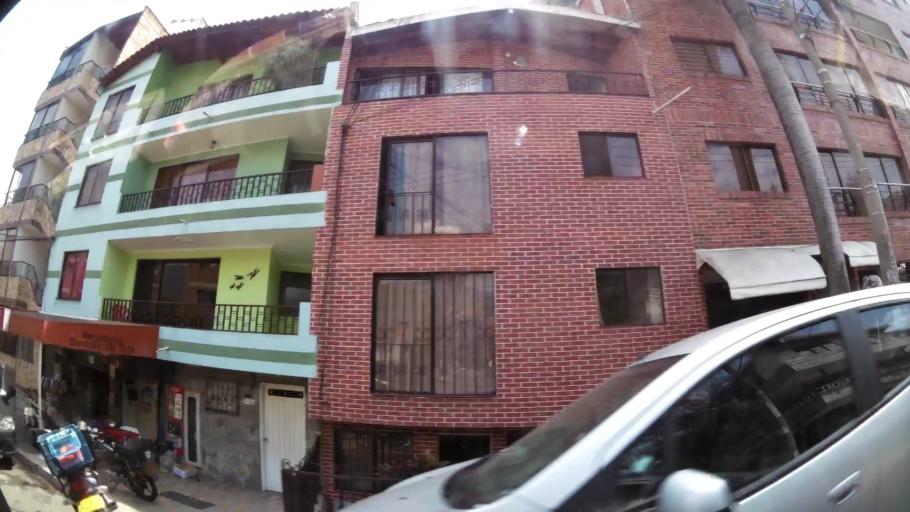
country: CO
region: Antioquia
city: Bello
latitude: 6.3186
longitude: -75.5650
